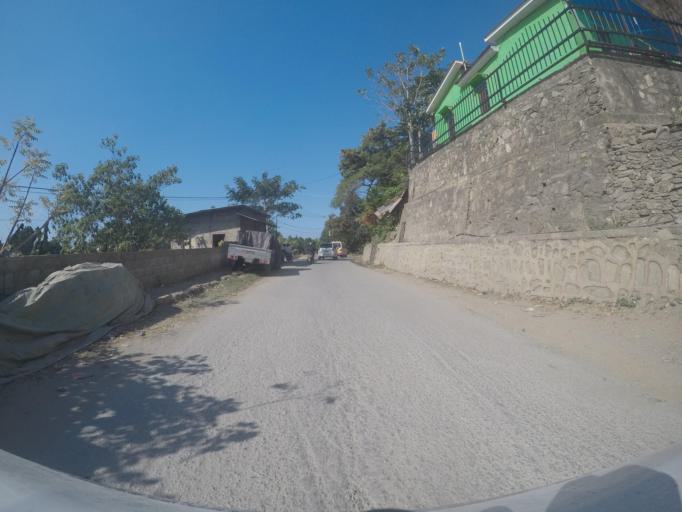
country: TL
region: Dili
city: Dili
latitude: -8.5690
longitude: 125.5455
